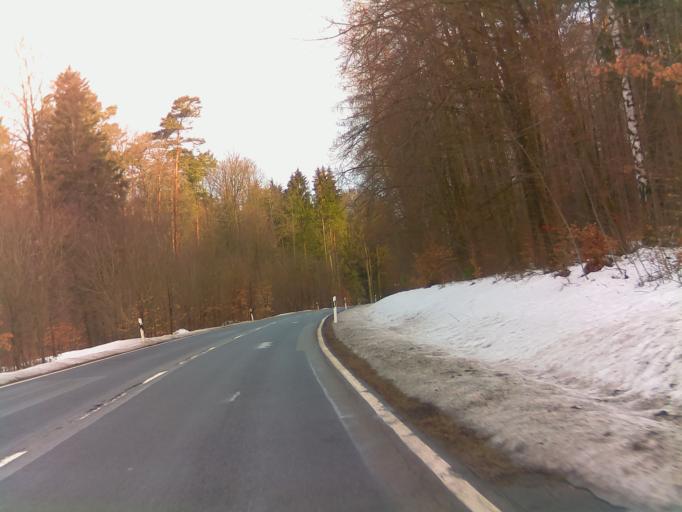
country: DE
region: Baden-Wuerttemberg
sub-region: Karlsruhe Region
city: Fahrenbach
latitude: 49.4892
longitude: 9.1458
